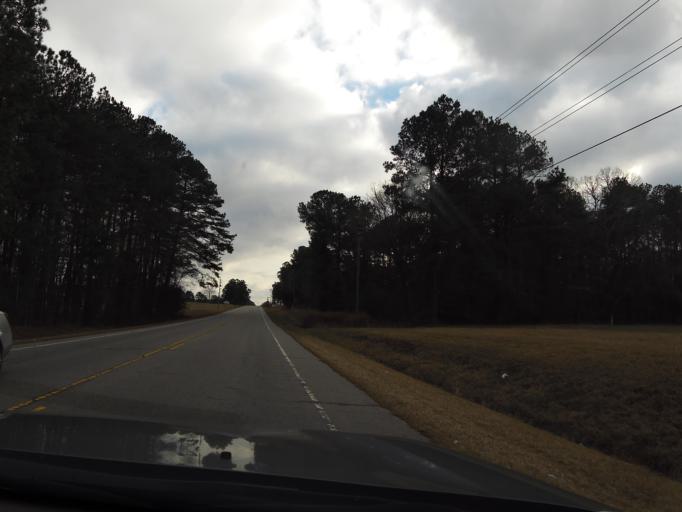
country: US
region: North Carolina
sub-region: Edgecombe County
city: Pinetops
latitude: 35.8391
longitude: -77.6613
